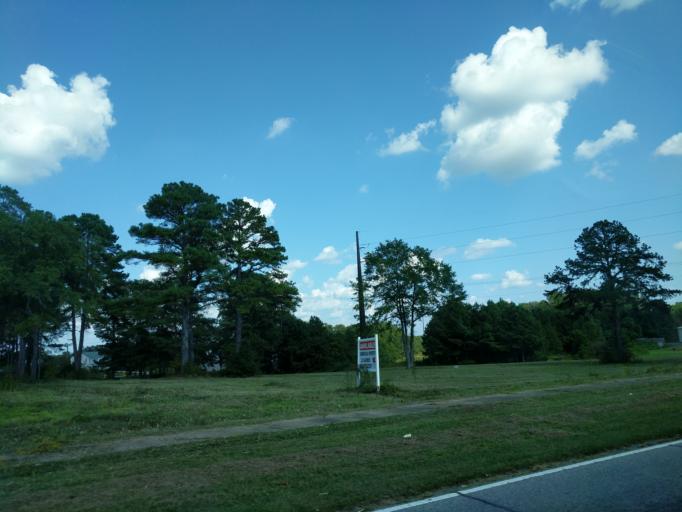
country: US
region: South Carolina
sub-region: Greenville County
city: Fountain Inn
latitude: 34.6168
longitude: -82.1215
